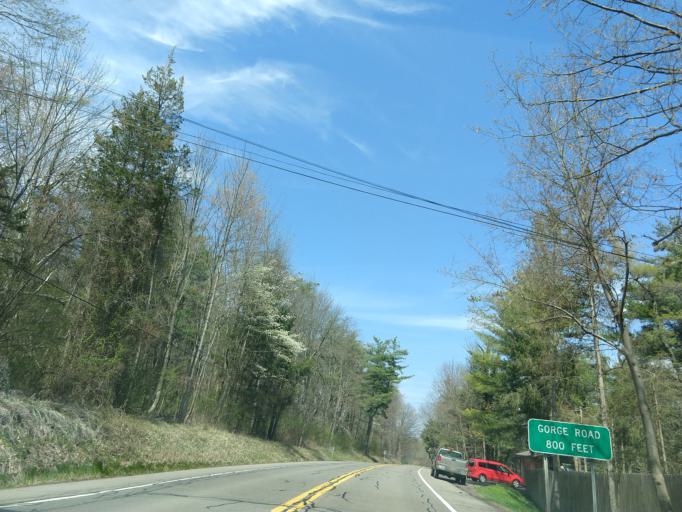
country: US
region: New York
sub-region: Tompkins County
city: Trumansburg
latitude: 42.5415
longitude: -76.5947
